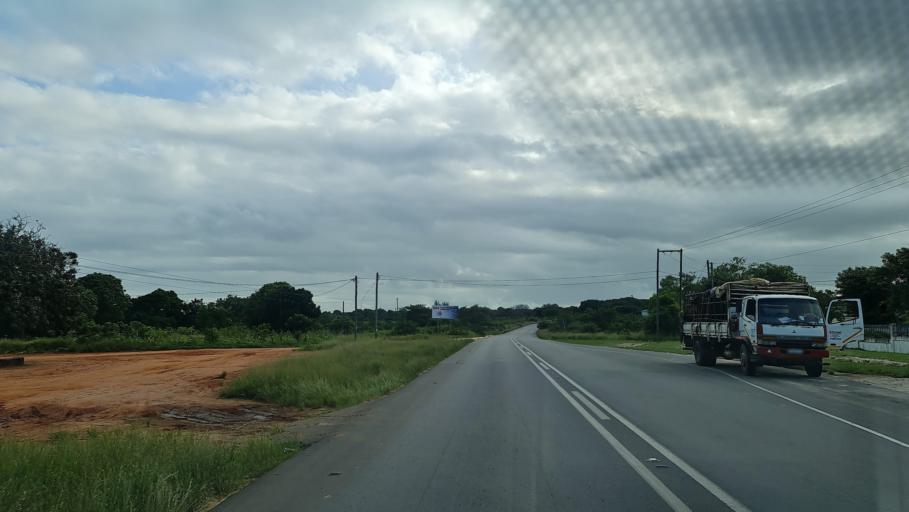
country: MZ
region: Maputo
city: Manhica
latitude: -25.4122
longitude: 32.7419
